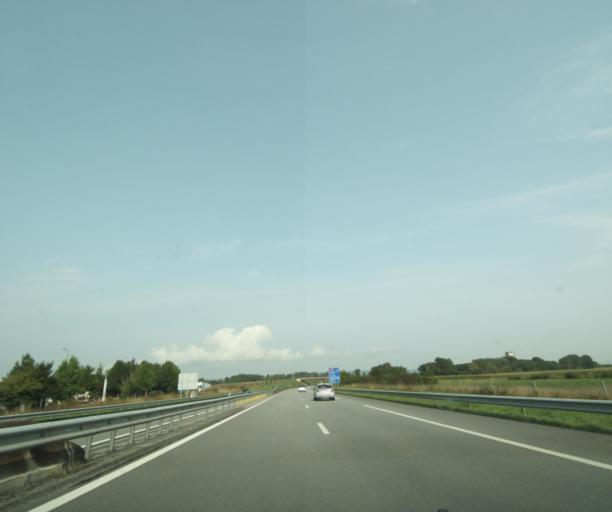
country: FR
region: Lower Normandy
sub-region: Departement de l'Orne
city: Valframbert
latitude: 48.4571
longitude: 0.1280
